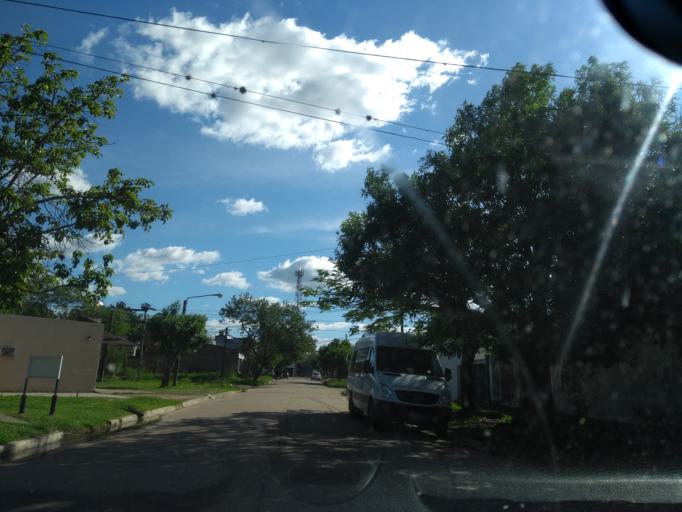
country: AR
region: Chaco
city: Barranqueras
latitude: -27.4739
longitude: -58.9583
